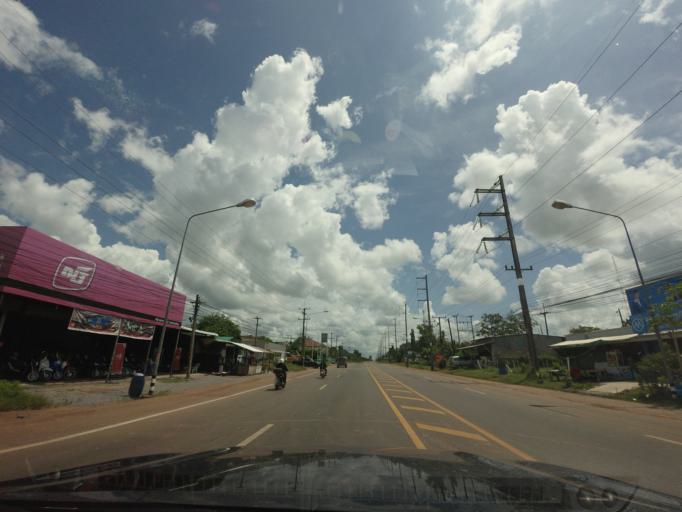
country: TH
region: Nong Khai
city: Sa Khrai
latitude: 17.5667
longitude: 102.6719
